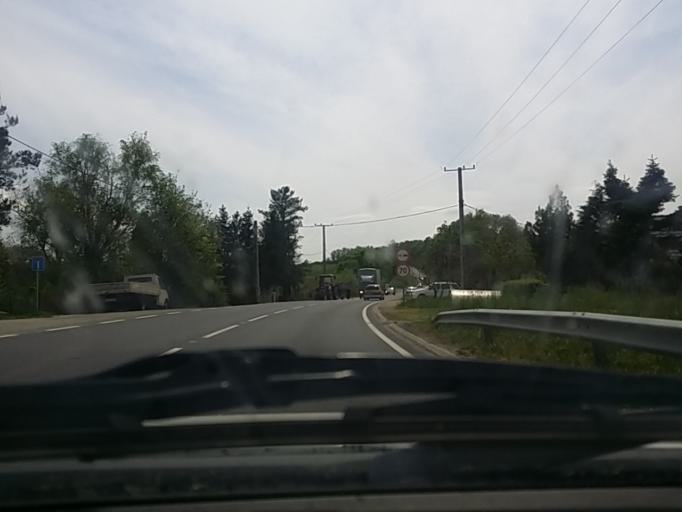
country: HU
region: Zala
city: Nagykanizsa
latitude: 46.4354
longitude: 17.0385
